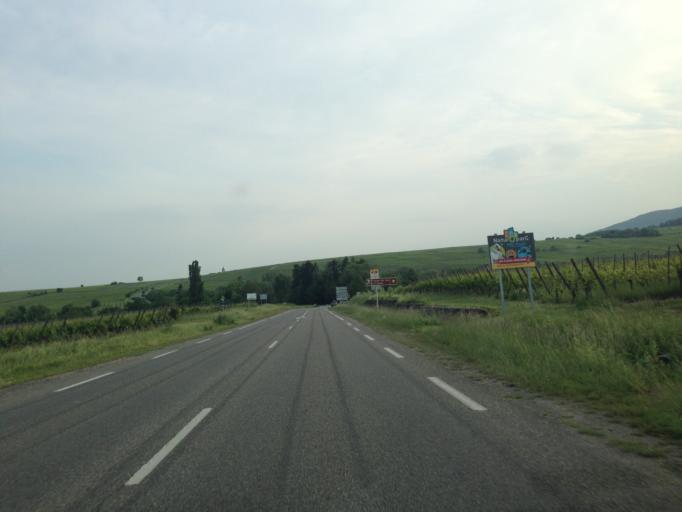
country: FR
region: Alsace
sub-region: Departement du Haut-Rhin
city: Ribeauville
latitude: 48.1847
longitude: 7.3247
